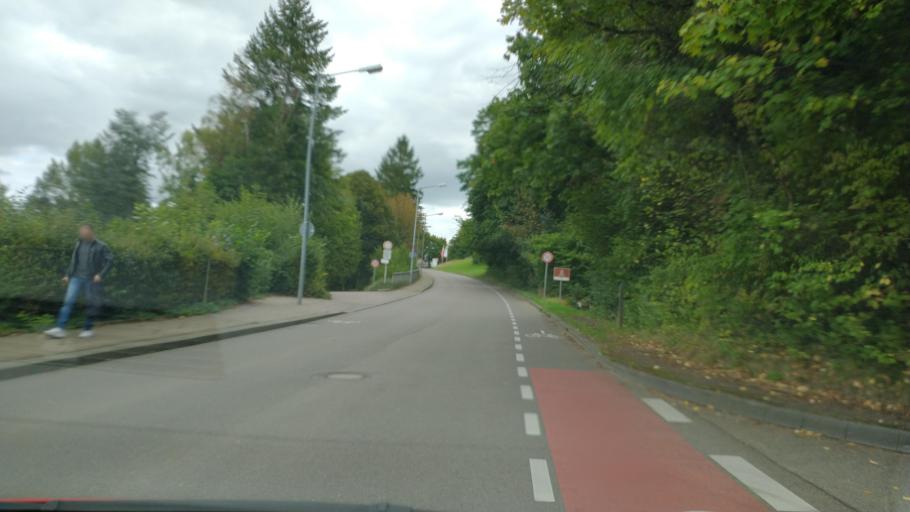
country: DE
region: Baden-Wuerttemberg
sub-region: Regierungsbezirk Stuttgart
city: Schwabisch Gmund
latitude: 48.7971
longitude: 9.8136
